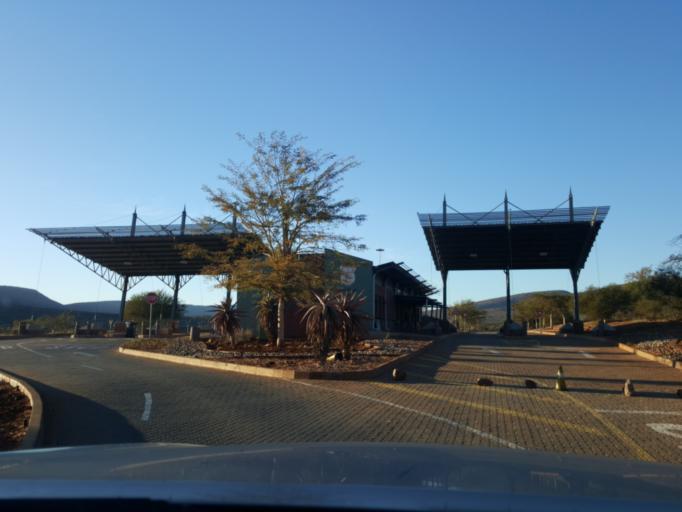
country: BW
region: South East
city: Lobatse
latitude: -25.2798
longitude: 25.7169
